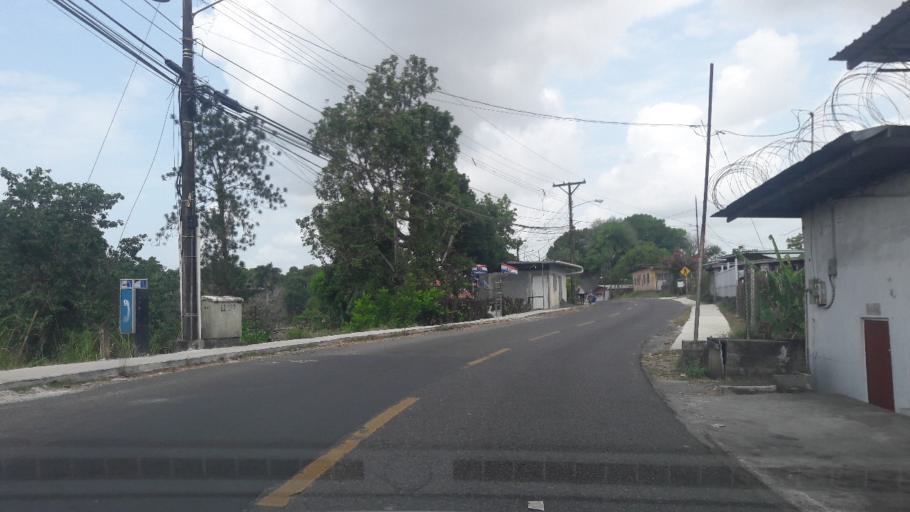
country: PA
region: Panama
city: Alcalde Diaz
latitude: 9.1152
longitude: -79.5552
